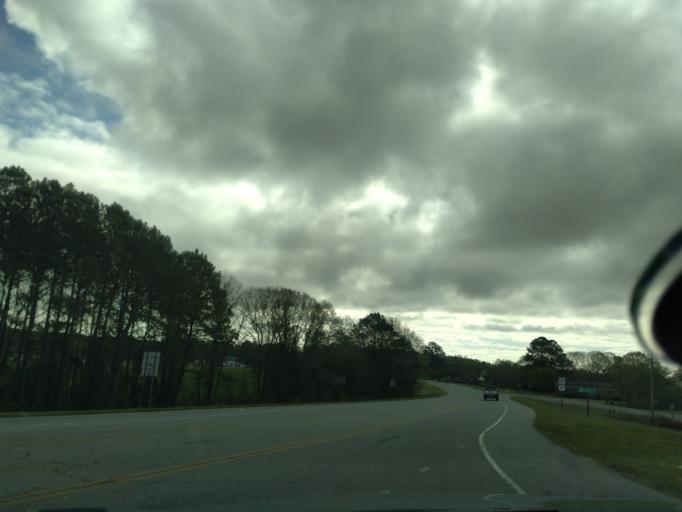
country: US
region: North Carolina
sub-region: Chowan County
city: Edenton
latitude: 36.0584
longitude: -76.6670
